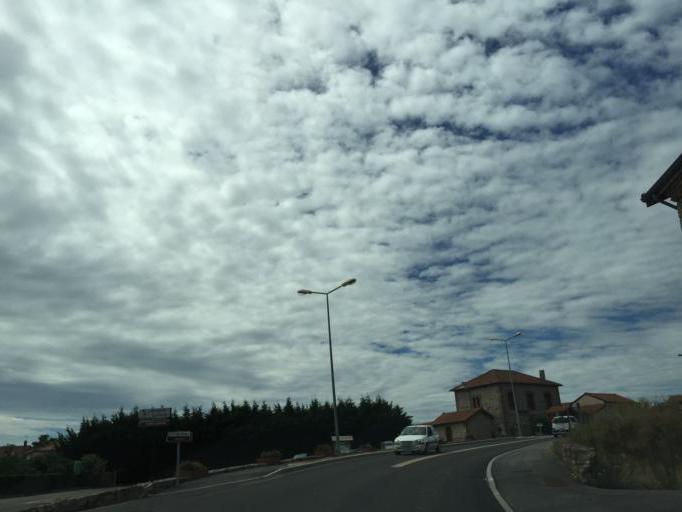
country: FR
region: Rhone-Alpes
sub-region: Departement de la Loire
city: Saint-Bonnet-le-Chateau
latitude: 45.4158
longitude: 4.0832
